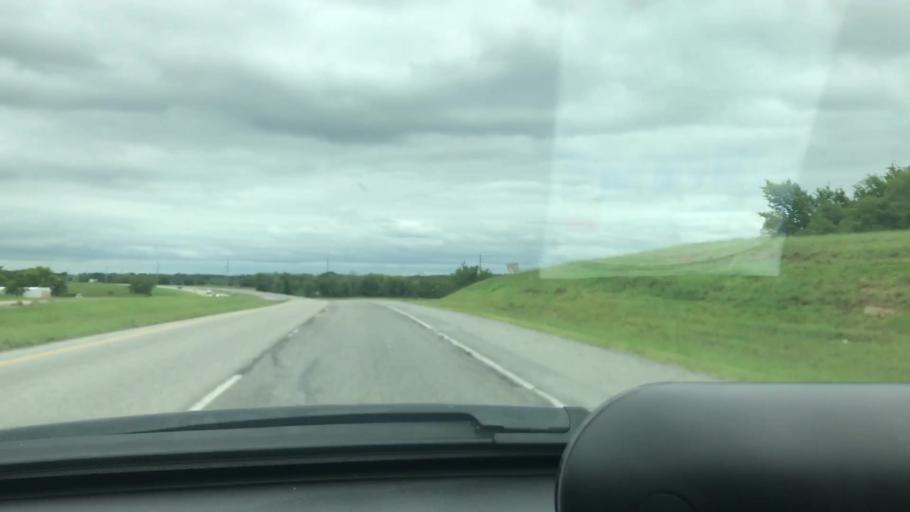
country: US
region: Oklahoma
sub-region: Wagoner County
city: Wagoner
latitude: 35.9919
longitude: -95.3715
